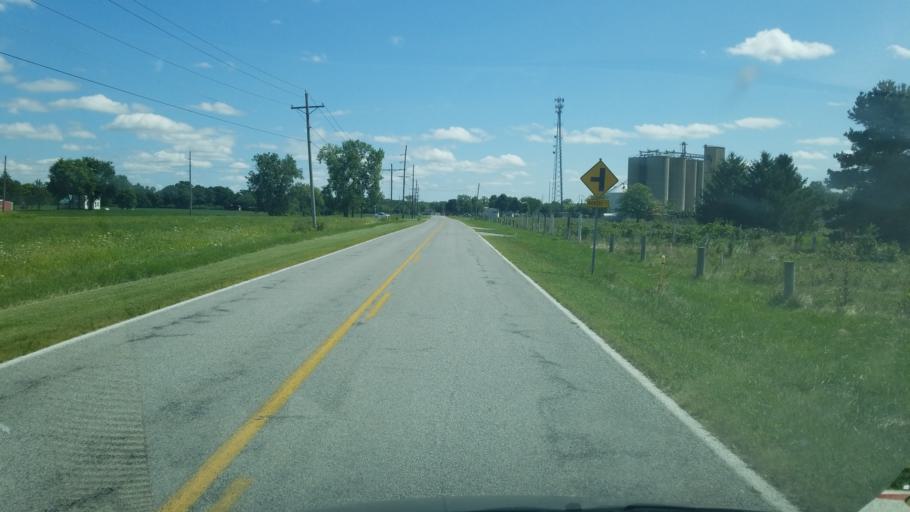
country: US
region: Ohio
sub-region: Wood County
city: Weston
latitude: 41.4189
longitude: -83.8672
